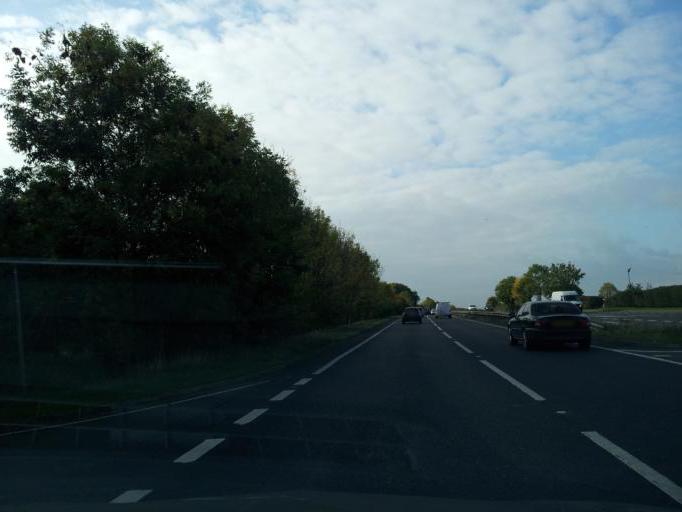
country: GB
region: England
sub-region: Northamptonshire
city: Silverstone
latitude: 52.0704
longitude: -1.0571
